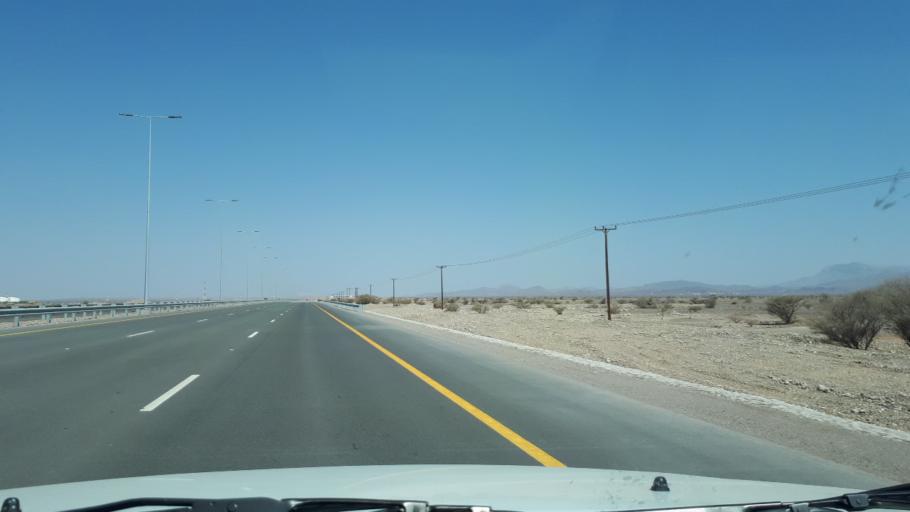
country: OM
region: Ash Sharqiyah
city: Badiyah
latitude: 22.3866
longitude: 59.0847
